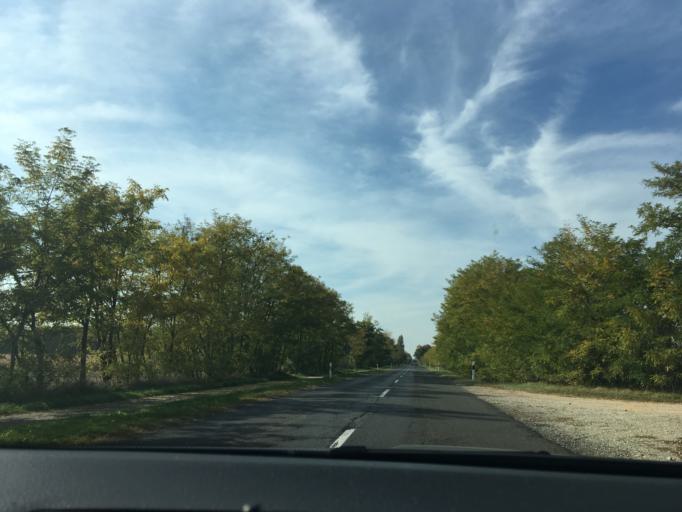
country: HU
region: Hajdu-Bihar
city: Vamospercs
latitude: 47.5256
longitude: 21.9425
